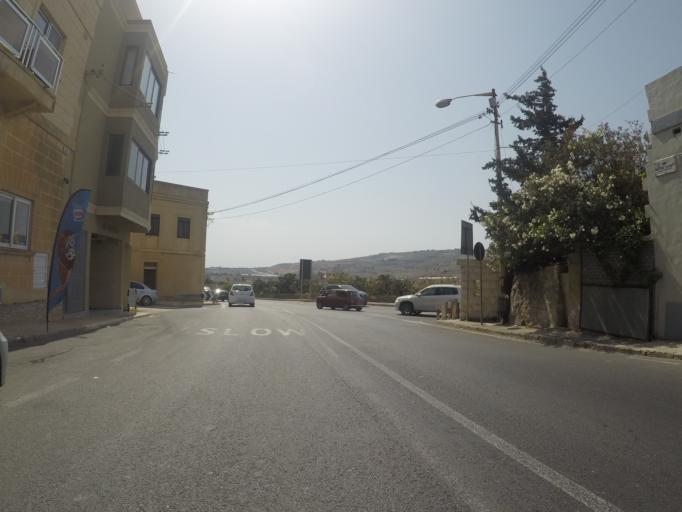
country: MT
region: L-Imgarr
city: Imgarr
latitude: 35.9190
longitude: 14.3803
